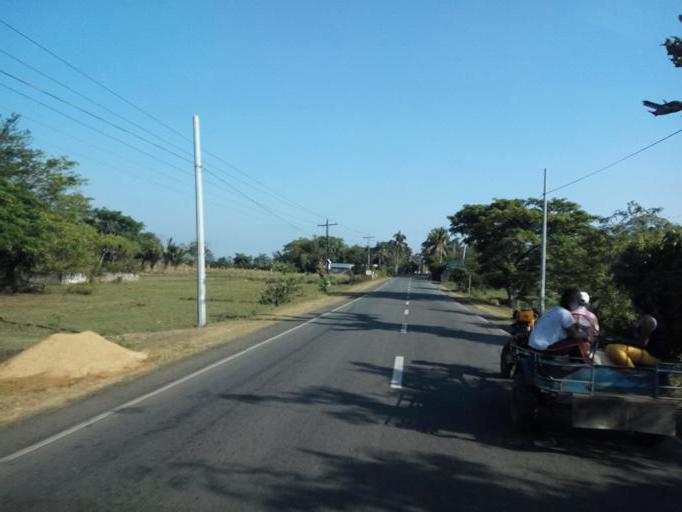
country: PH
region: Cagayan Valley
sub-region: Province of Cagayan
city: Amulung
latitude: 17.8268
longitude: 121.7251
